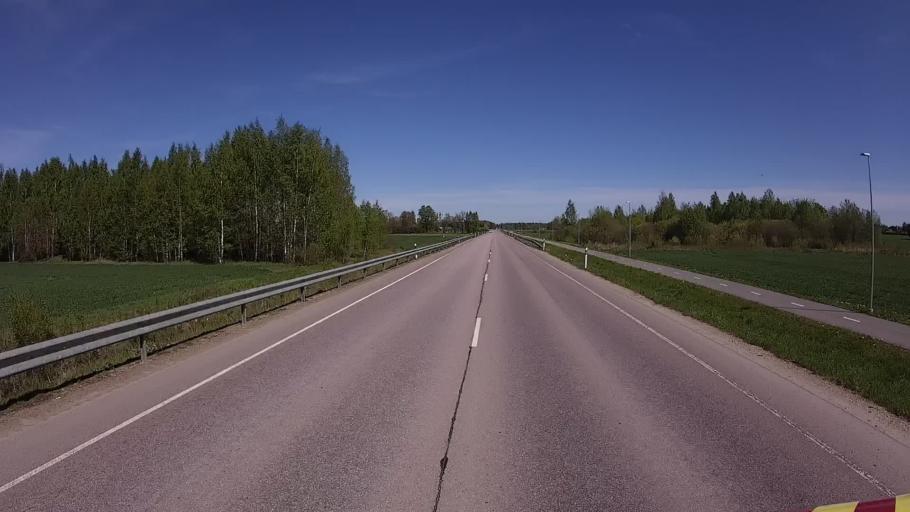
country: EE
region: Polvamaa
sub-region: Polva linn
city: Polva
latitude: 58.0756
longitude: 27.0885
